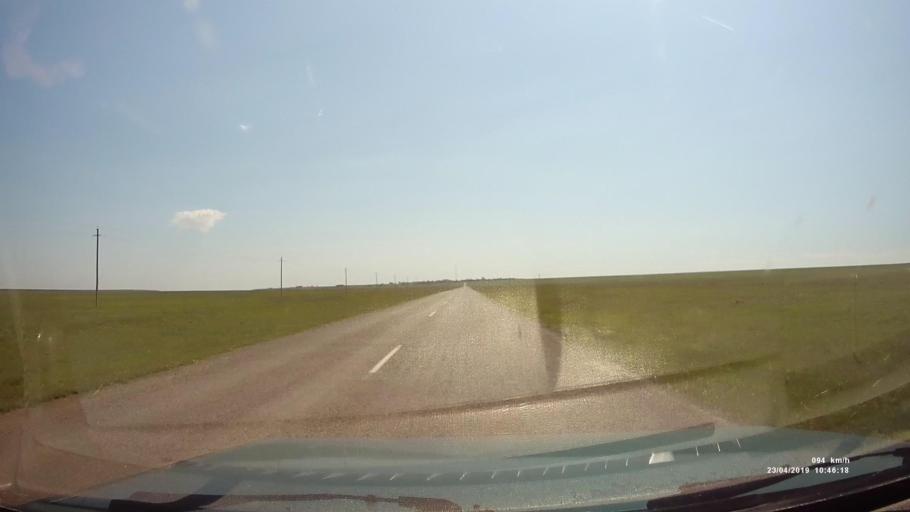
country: RU
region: Kalmykiya
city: Yashalta
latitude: 46.4441
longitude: 42.6889
